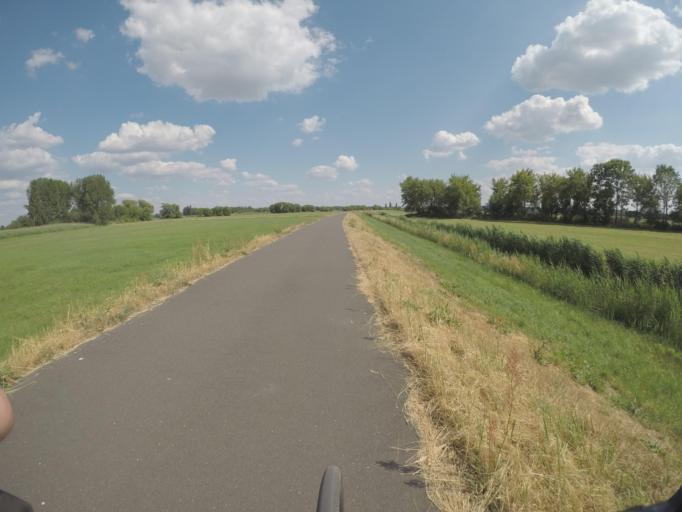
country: DE
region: Brandenburg
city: Ketzin
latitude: 52.4551
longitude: 12.8695
